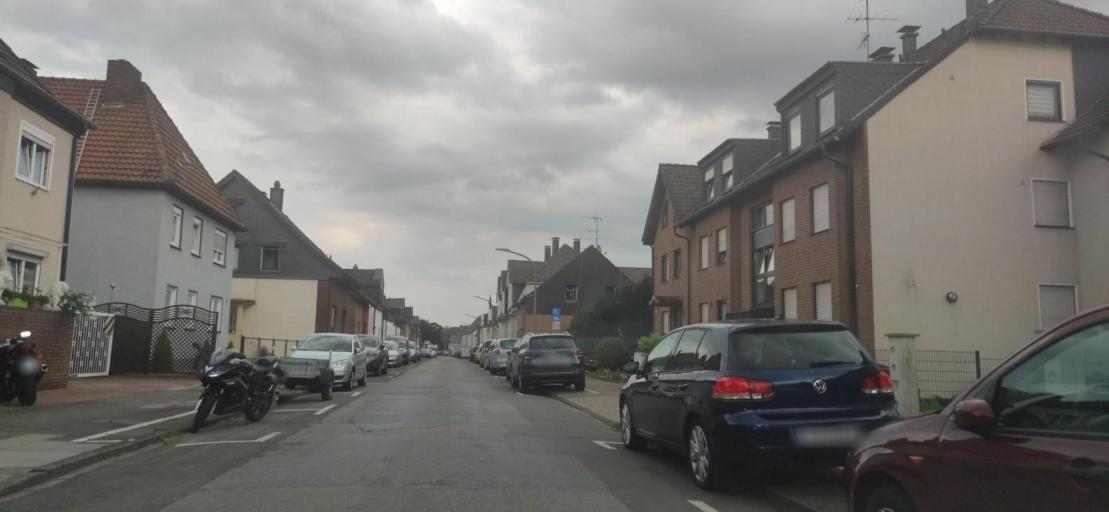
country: DE
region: North Rhine-Westphalia
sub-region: Regierungsbezirk Munster
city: Bottrop
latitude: 51.5255
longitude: 6.9392
